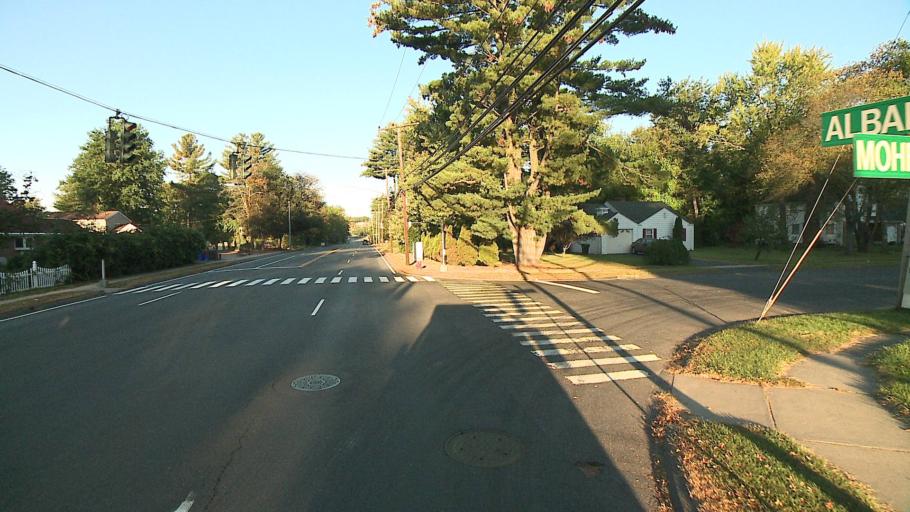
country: US
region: Connecticut
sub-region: Hartford County
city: West Hartford
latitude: 41.7865
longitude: -72.7352
